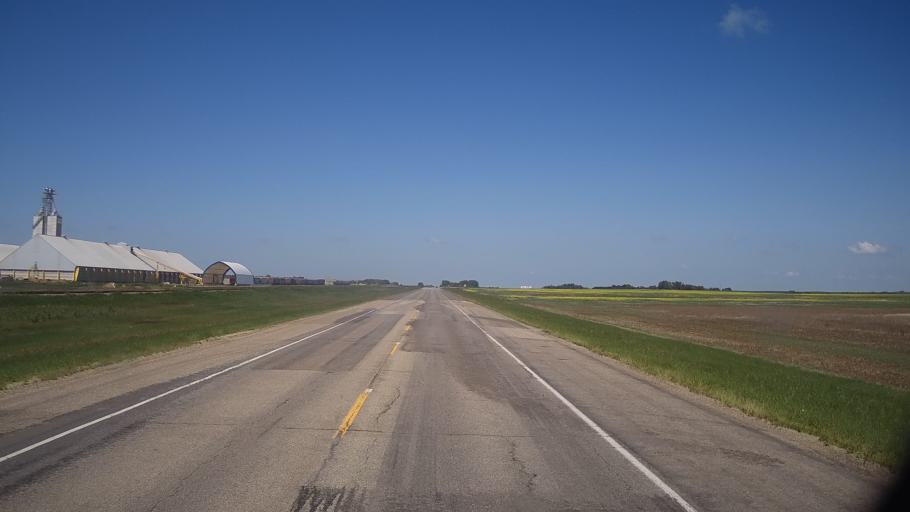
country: CA
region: Saskatchewan
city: Saskatoon
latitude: 51.9928
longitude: -106.0855
